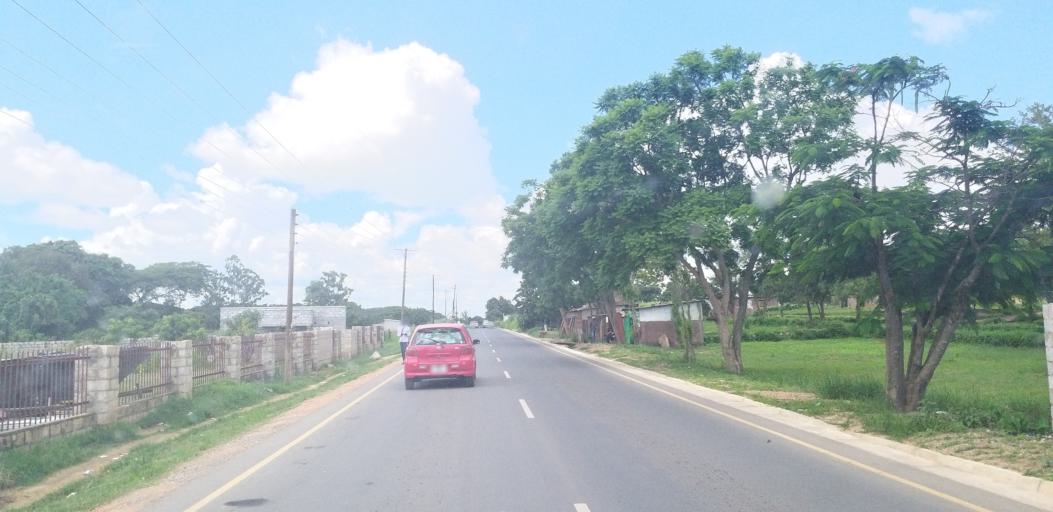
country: ZM
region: Lusaka
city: Lusaka
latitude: -15.3366
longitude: 28.3297
